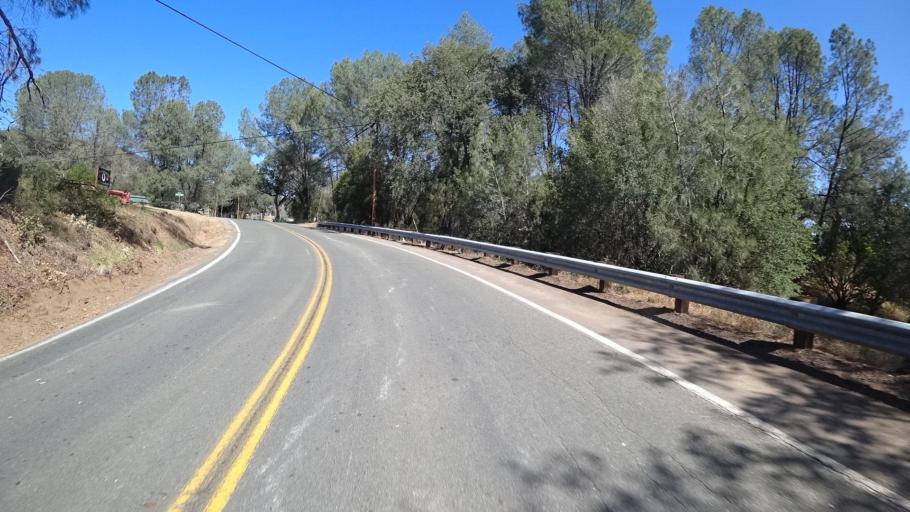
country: US
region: California
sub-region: Lake County
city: Clearlake Oaks
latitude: 39.0566
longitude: -122.5881
